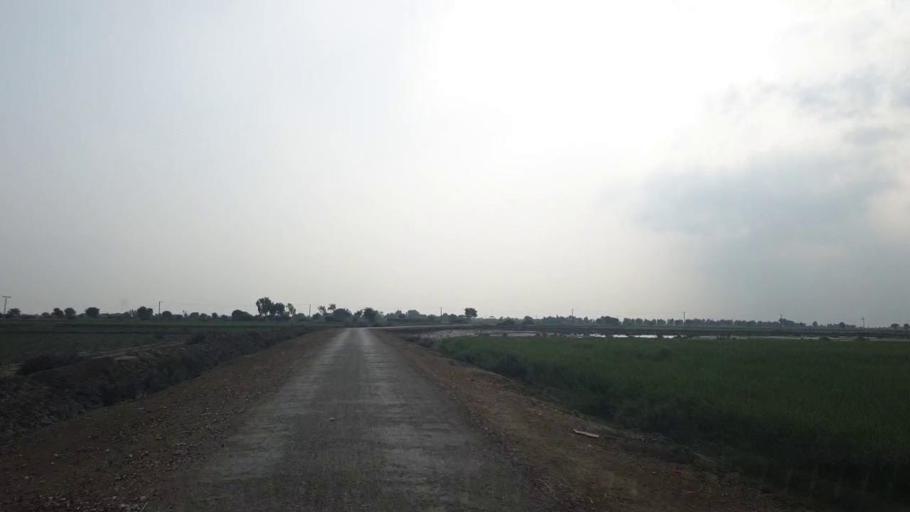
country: PK
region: Sindh
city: Badin
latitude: 24.6460
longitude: 68.6977
